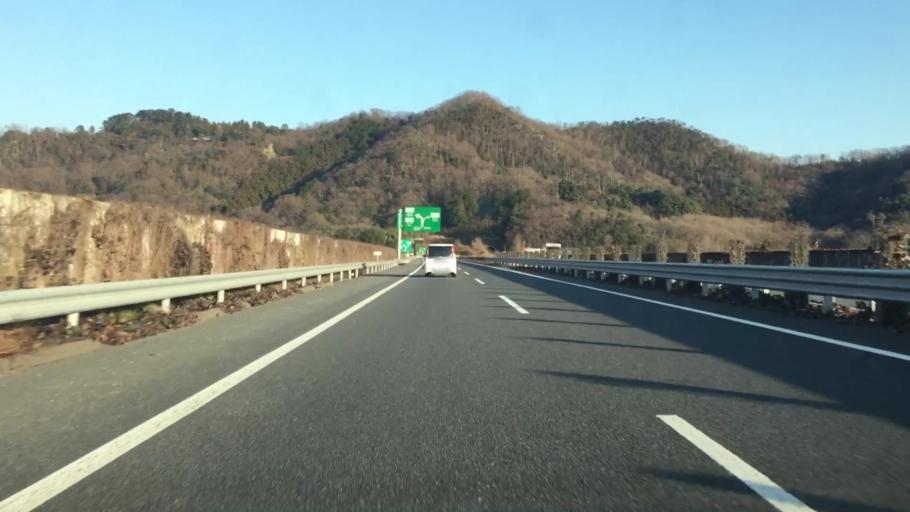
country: JP
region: Tochigi
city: Tanuma
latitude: 36.3527
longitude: 139.5853
